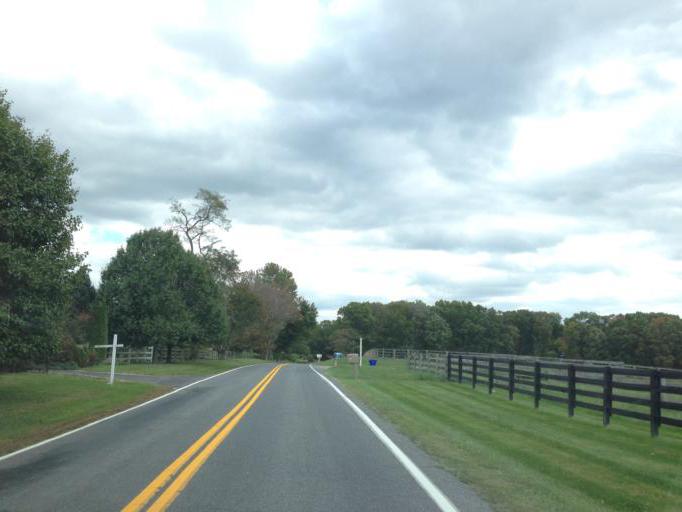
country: US
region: Maryland
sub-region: Montgomery County
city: Olney
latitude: 39.2730
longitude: -77.0804
